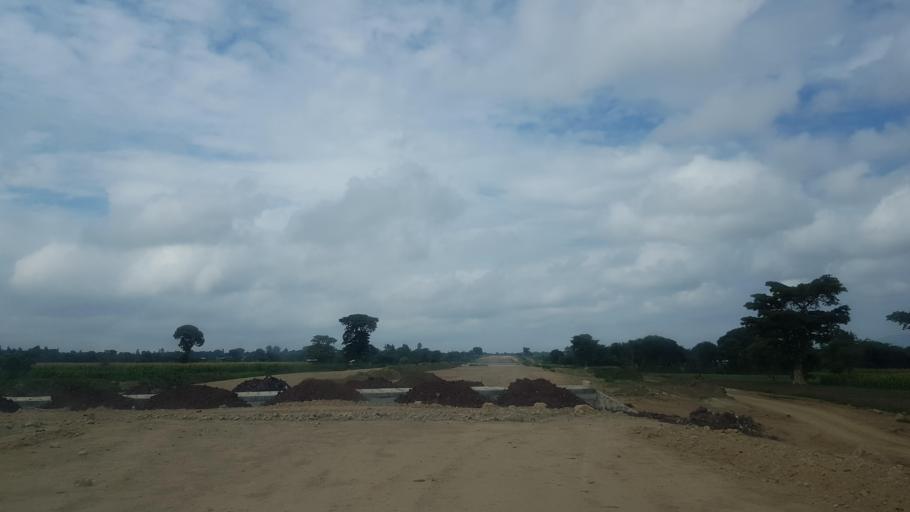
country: ET
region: Oromiya
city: Shashemene
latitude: 7.2833
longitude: 38.6072
